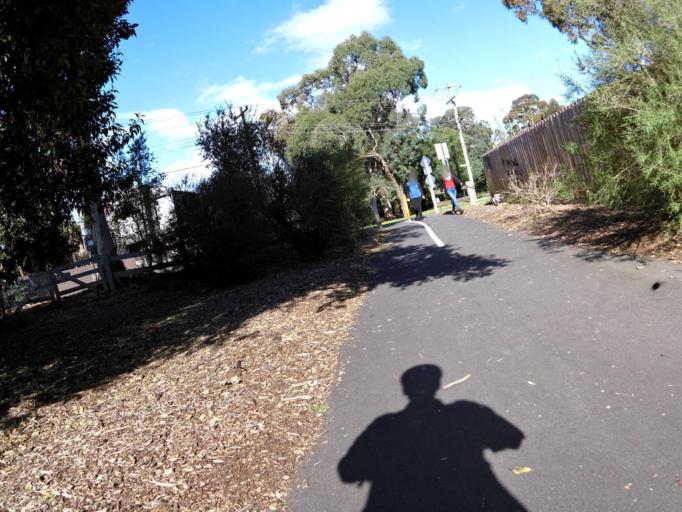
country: AU
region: Victoria
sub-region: Whitehorse
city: Box Hill North
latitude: -37.8027
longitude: 145.1229
